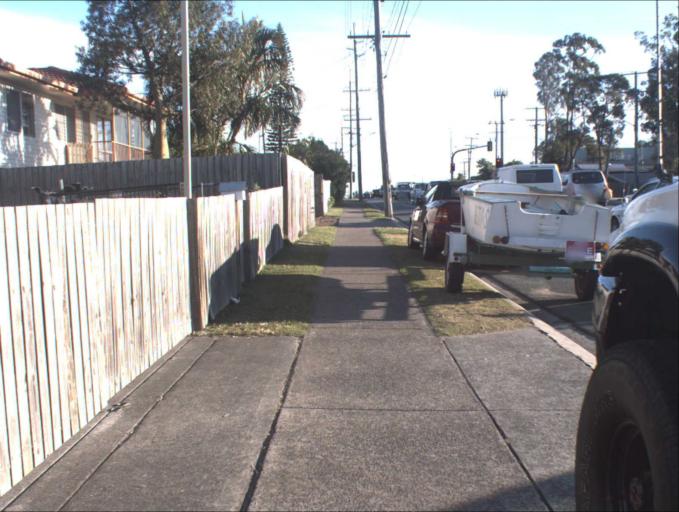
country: AU
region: Queensland
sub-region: Logan
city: Logan City
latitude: -27.6364
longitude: 153.1190
